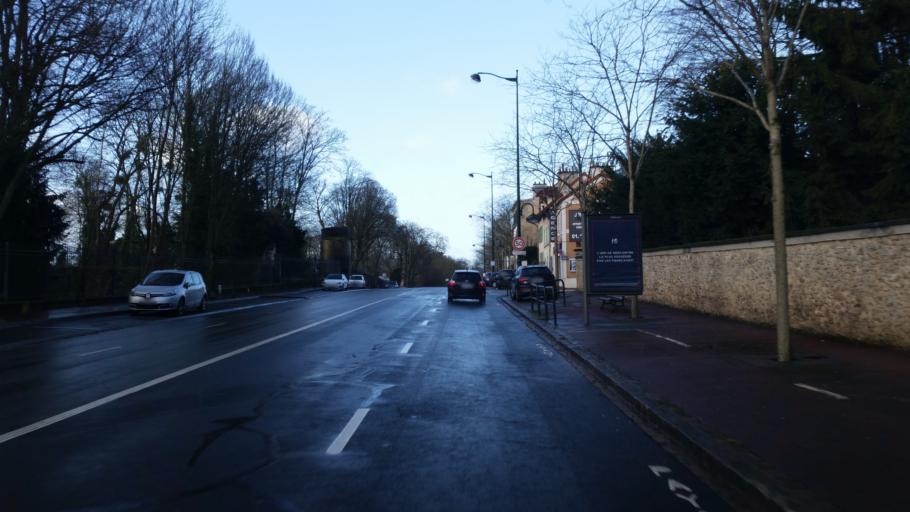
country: FR
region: Ile-de-France
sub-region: Departement des Hauts-de-Seine
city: Garches
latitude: 48.8383
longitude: 2.1828
